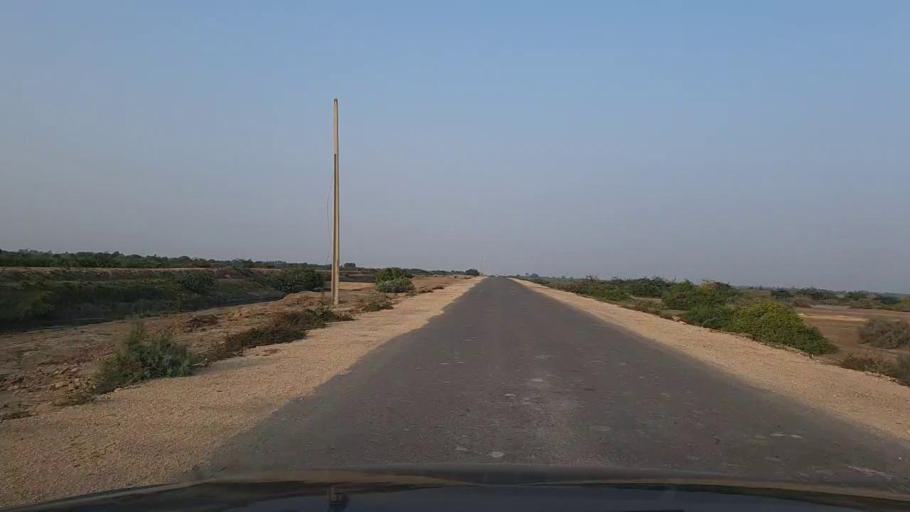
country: PK
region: Sindh
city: Mirpur Sakro
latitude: 24.4659
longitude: 67.7979
